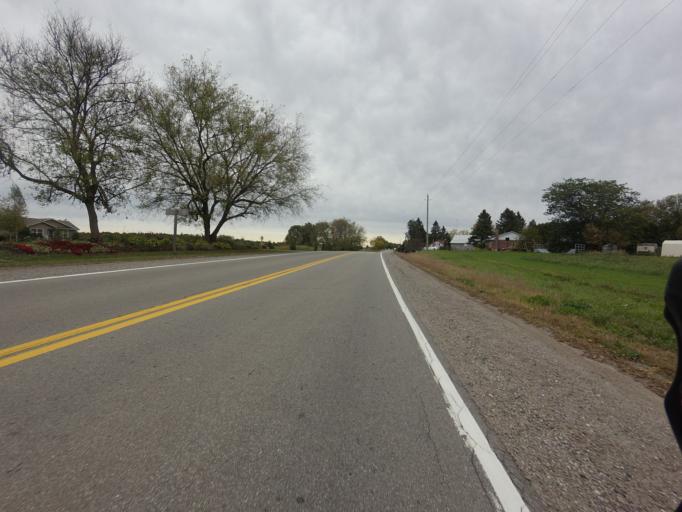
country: CA
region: Ontario
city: Gananoque
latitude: 44.5245
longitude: -76.1559
